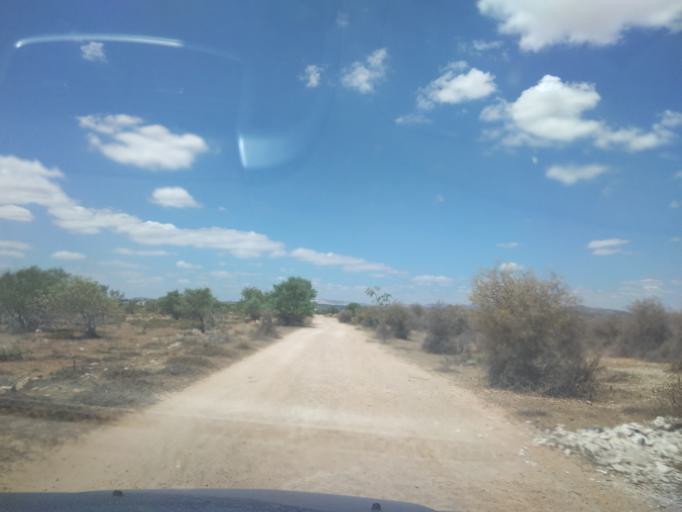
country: TN
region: Susah
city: Harqalah
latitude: 36.1664
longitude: 10.4418
